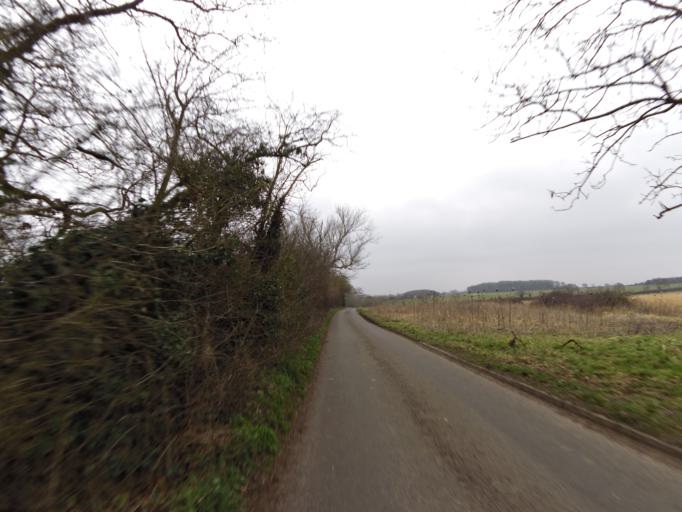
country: GB
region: England
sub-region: Suffolk
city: Framlingham
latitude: 52.2318
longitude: 1.3531
